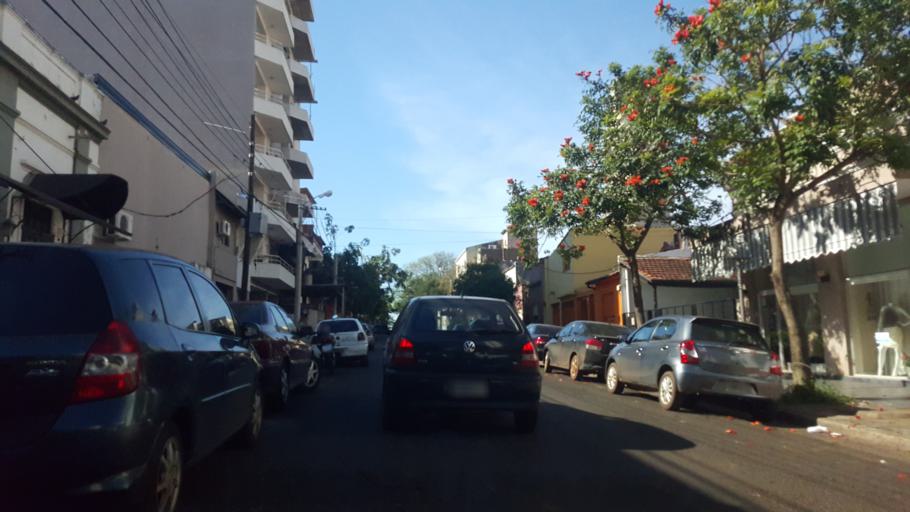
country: AR
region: Misiones
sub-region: Departamento de Capital
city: Posadas
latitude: -27.3645
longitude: -55.8902
